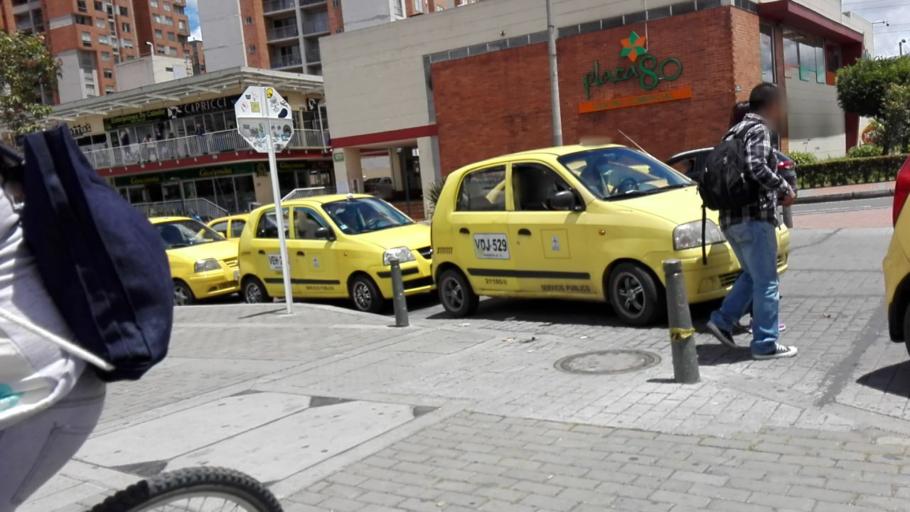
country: CO
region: Bogota D.C.
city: Barrio San Luis
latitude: 4.6936
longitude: -74.0863
